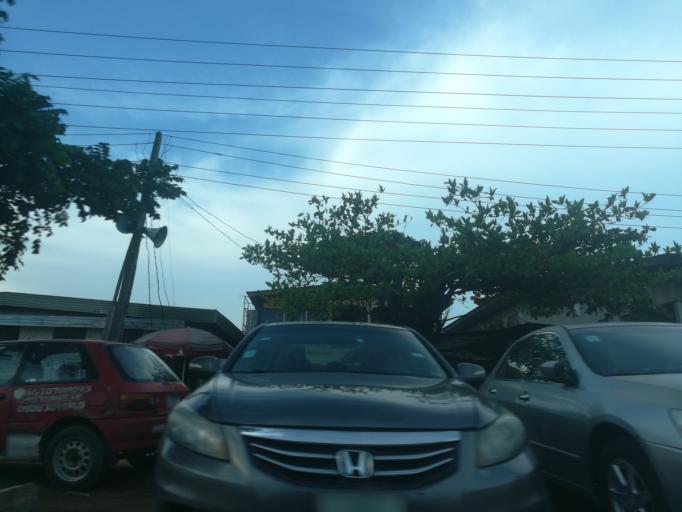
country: NG
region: Lagos
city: Ikorodu
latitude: 6.6247
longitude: 3.4933
